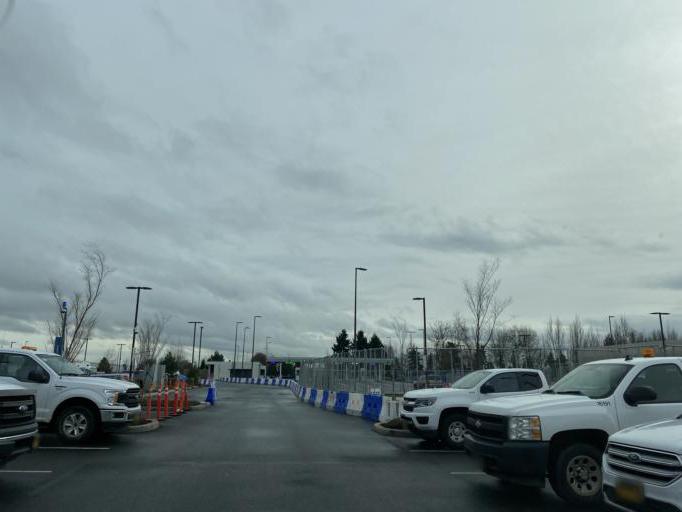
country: US
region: Washington
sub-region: Clark County
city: Walnut Grove
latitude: 45.5863
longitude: -122.5873
